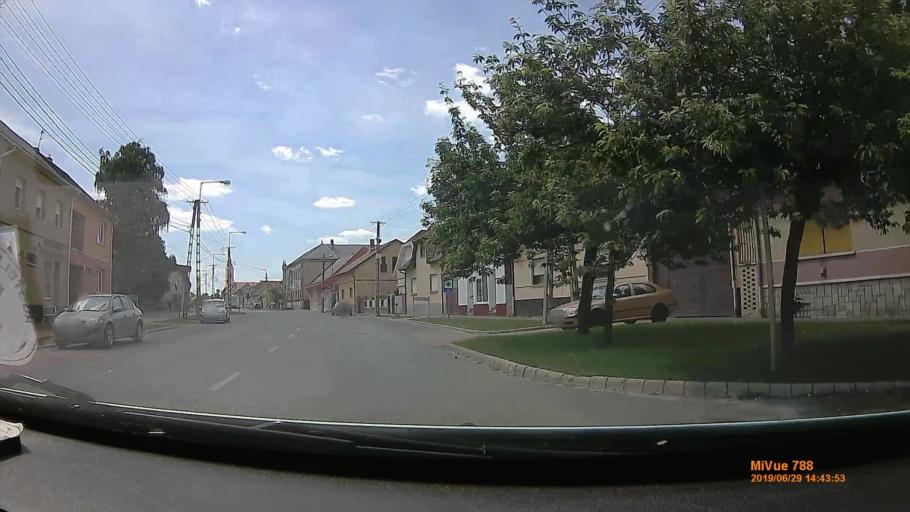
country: HU
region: Komarom-Esztergom
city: Nyergesujfalu
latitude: 47.7614
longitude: 18.5531
